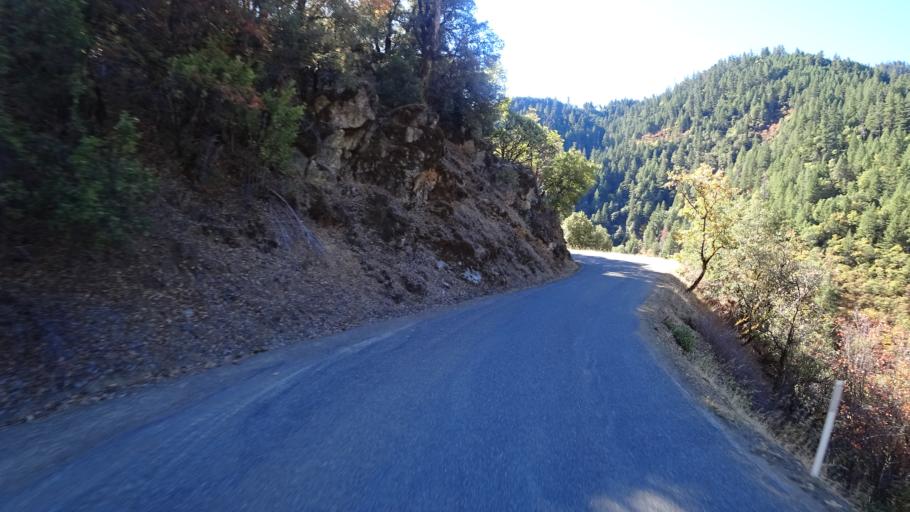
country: US
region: California
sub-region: Humboldt County
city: Willow Creek
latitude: 41.1678
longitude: -123.2147
